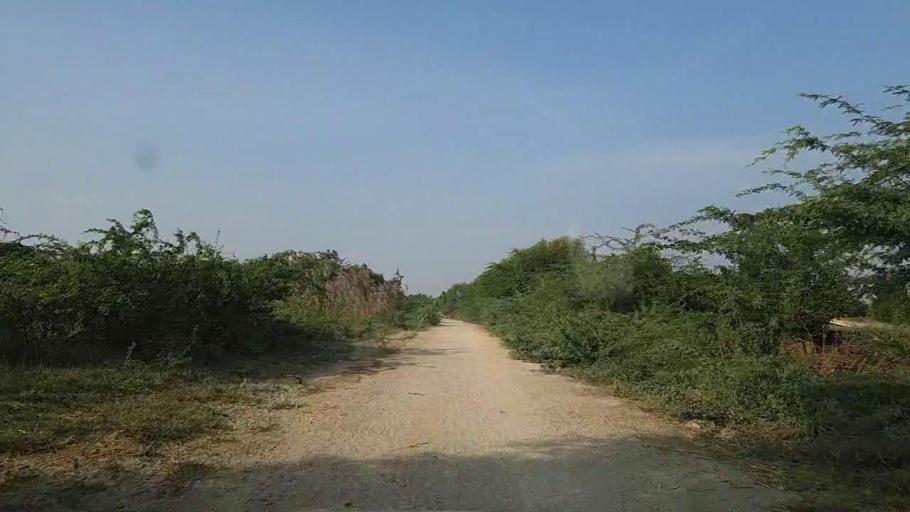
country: PK
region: Sindh
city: Mirpur Sakro
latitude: 24.5893
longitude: 67.6495
